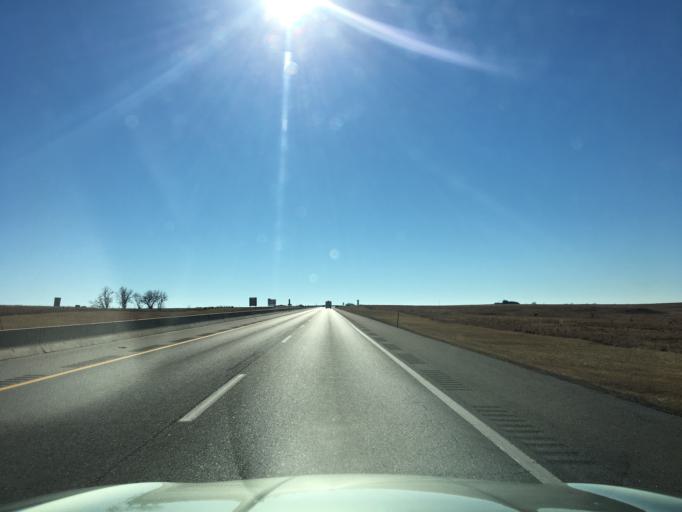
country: US
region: Kansas
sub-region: Sumner County
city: Wellington
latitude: 37.0522
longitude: -97.3384
